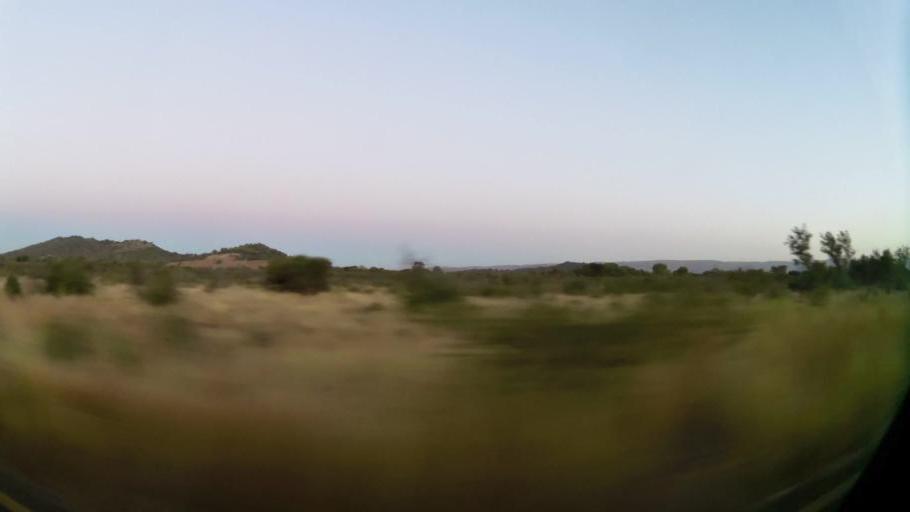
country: ZA
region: North-West
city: Ga-Rankuwa
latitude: -25.6320
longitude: 27.9573
